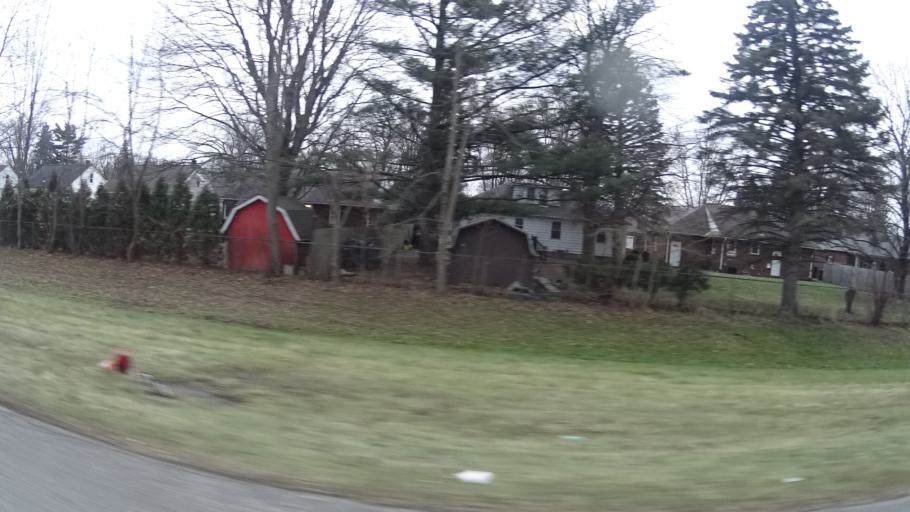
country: US
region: Ohio
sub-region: Lorain County
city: Elyria
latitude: 41.3854
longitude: -82.1328
